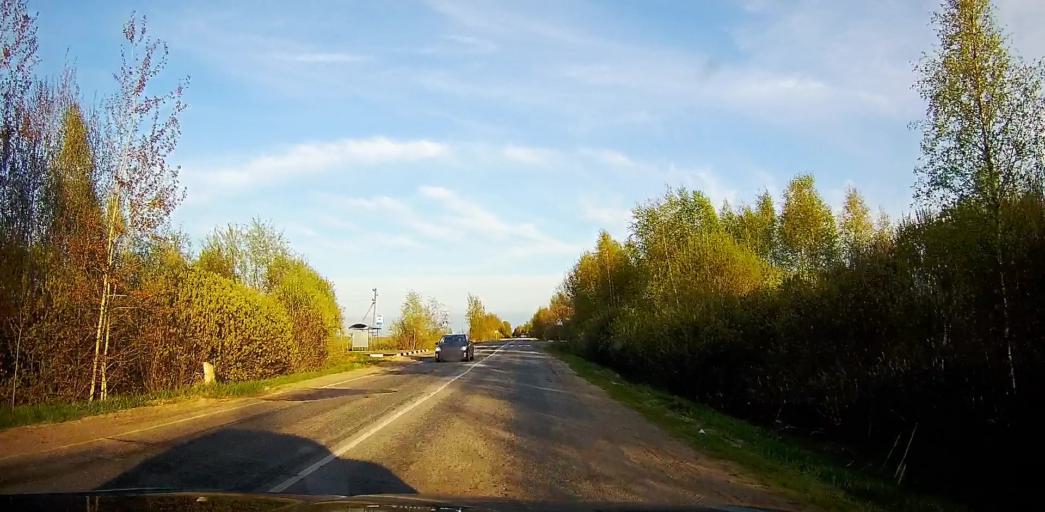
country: RU
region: Moskovskaya
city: Bronnitsy
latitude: 55.2783
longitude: 38.2195
